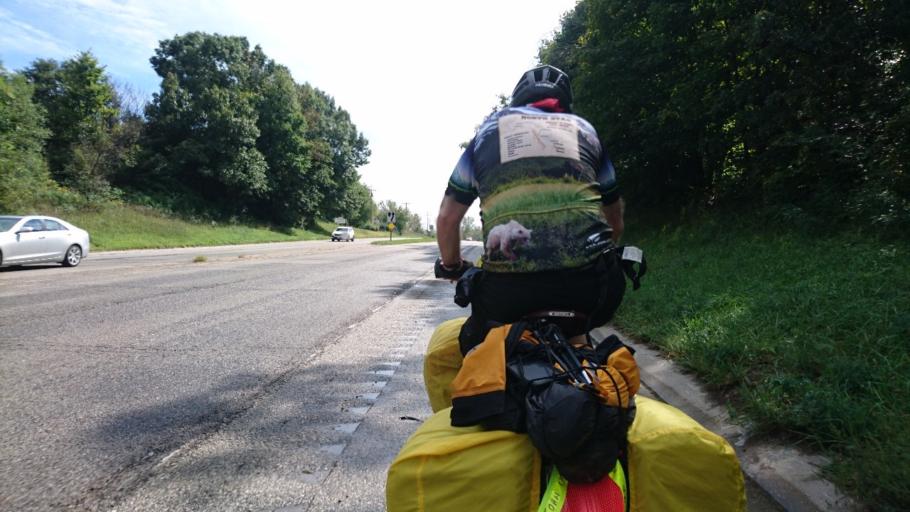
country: US
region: Illinois
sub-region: Sangamon County
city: Sherman
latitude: 39.8628
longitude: -89.6140
